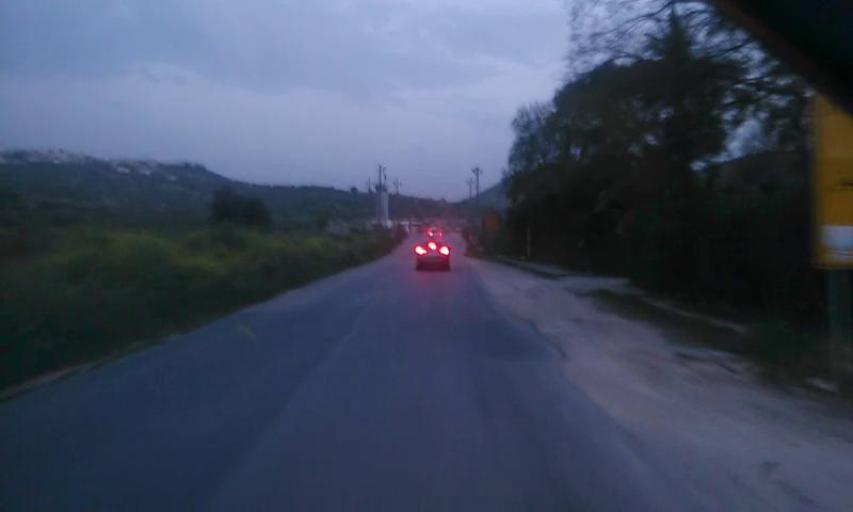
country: PS
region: West Bank
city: Ramin
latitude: 32.2912
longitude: 35.1352
